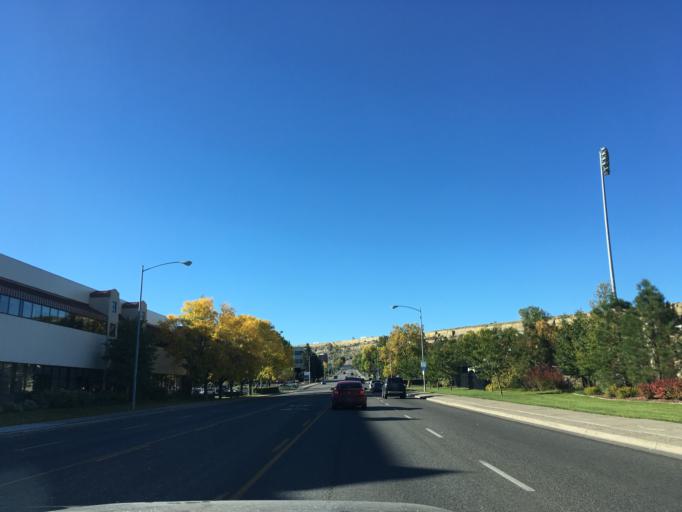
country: US
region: Montana
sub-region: Yellowstone County
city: Billings
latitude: 45.7900
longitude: -108.5117
